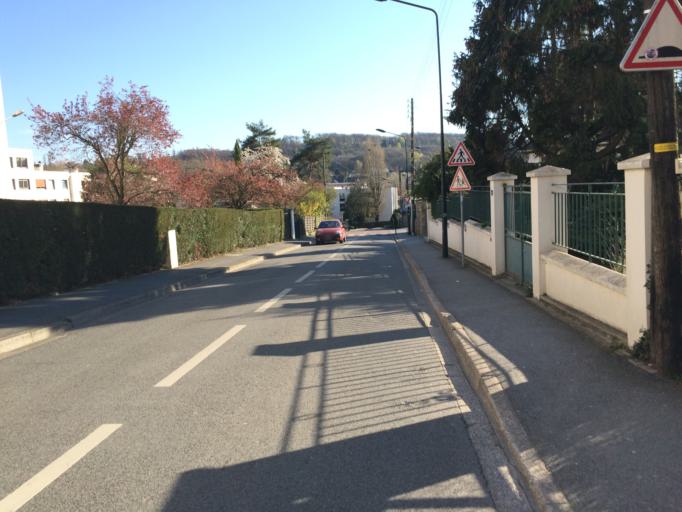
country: FR
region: Ile-de-France
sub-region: Departement de l'Essonne
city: Villebon-sur-Yvette
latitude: 48.7043
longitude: 2.2376
